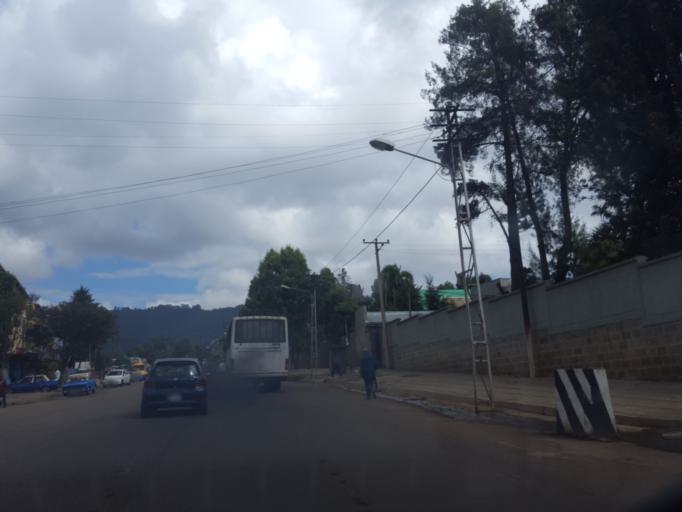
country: ET
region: Adis Abeba
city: Addis Ababa
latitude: 9.0593
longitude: 38.7623
